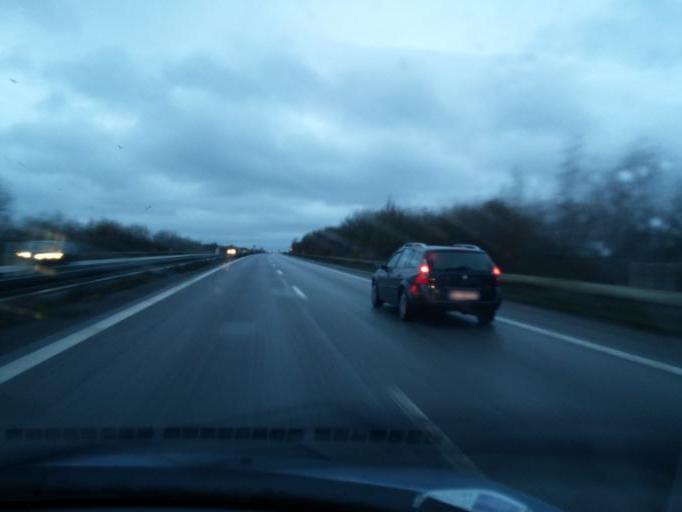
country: DK
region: South Denmark
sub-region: Odense Kommune
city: Bellinge
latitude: 55.3701
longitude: 10.3060
